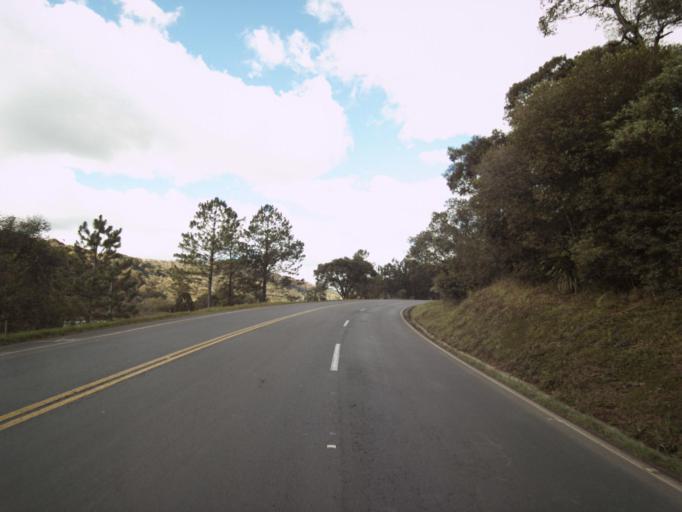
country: BR
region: Santa Catarina
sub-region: Joacaba
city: Joacaba
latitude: -27.0544
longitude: -51.6953
